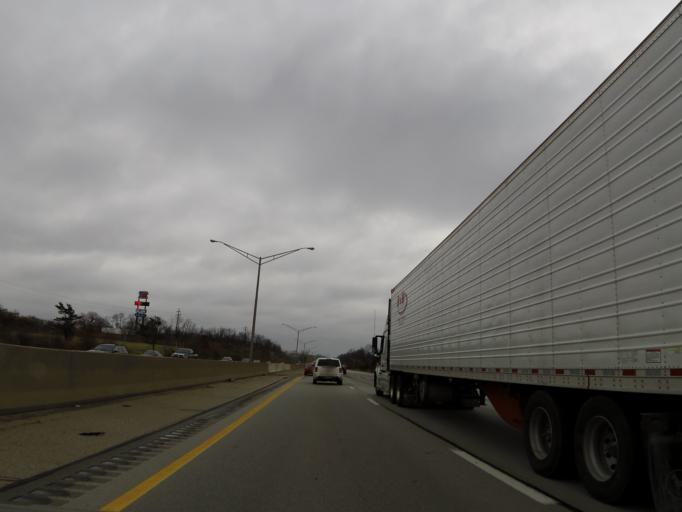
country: US
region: Kentucky
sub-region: Boone County
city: Walton
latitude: 38.9185
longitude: -84.6293
